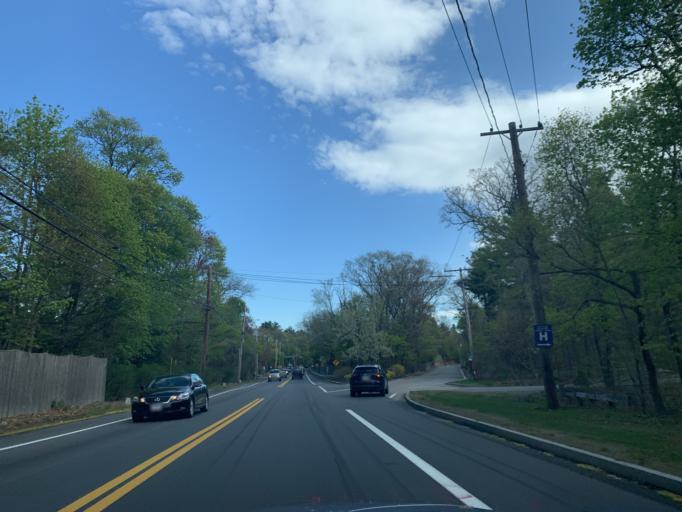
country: US
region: Massachusetts
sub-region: Norfolk County
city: Dedham
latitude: 42.2207
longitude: -71.1188
